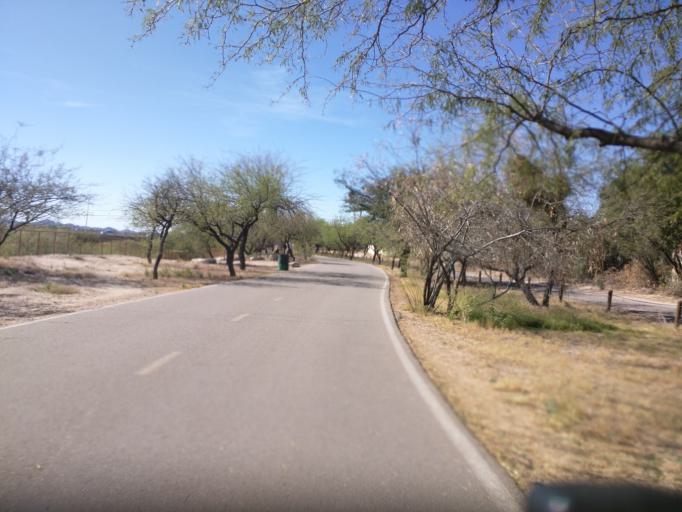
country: US
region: Arizona
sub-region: Pima County
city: Flowing Wells
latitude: 32.2944
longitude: -110.9934
